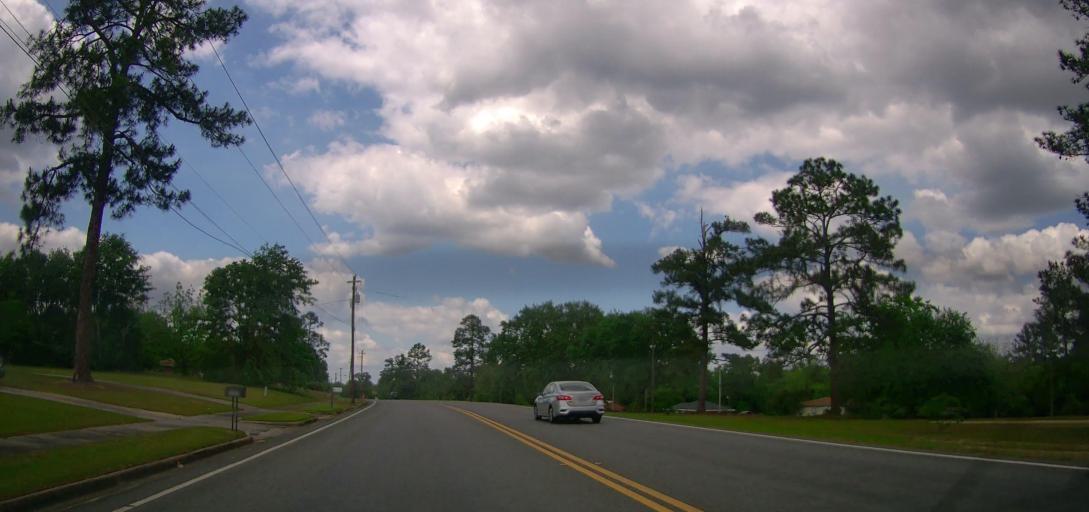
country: US
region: Georgia
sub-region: Treutlen County
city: Soperton
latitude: 32.3667
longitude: -82.5827
